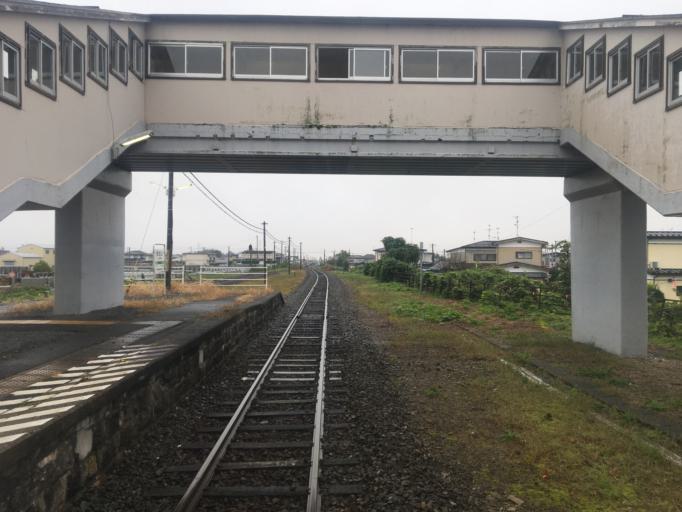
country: JP
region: Miyagi
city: Furukawa
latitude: 38.6521
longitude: 140.8718
